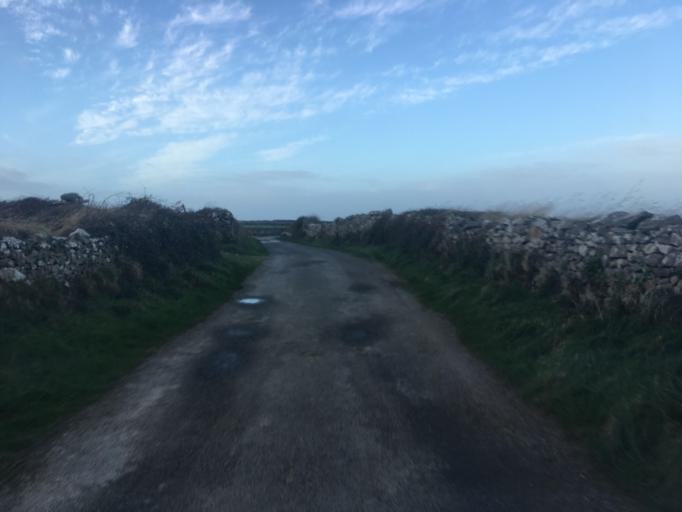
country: FR
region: Lower Normandy
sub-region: Departement de la Manche
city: Beaumont-Hague
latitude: 49.7215
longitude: -1.9218
